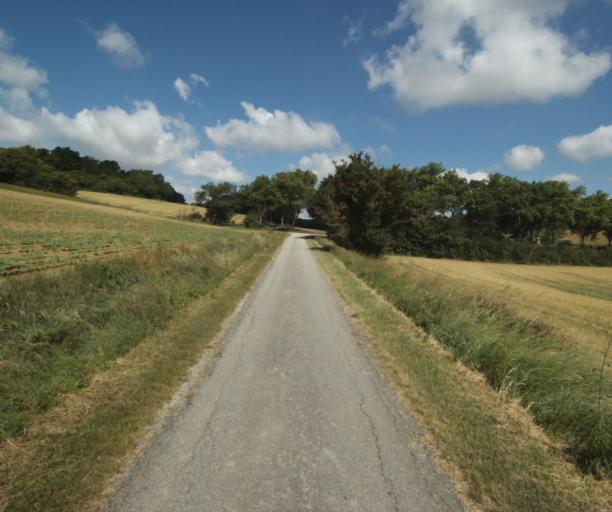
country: FR
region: Midi-Pyrenees
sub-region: Departement de la Haute-Garonne
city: Saint-Felix-Lauragais
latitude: 43.4478
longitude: 1.9022
